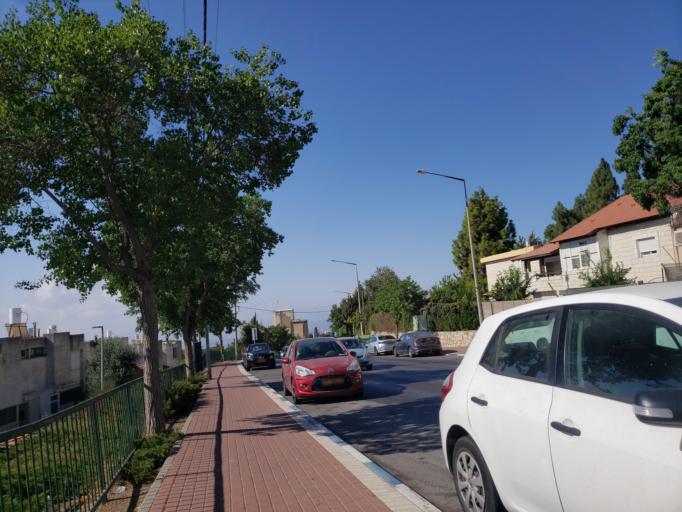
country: IL
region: Northern District
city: Safed
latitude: 32.9626
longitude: 35.4990
